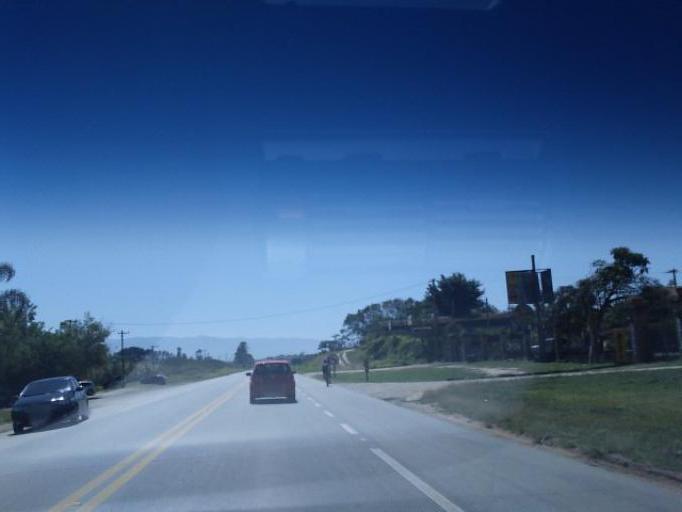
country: BR
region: Sao Paulo
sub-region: Tremembe
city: Tremembe
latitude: -22.9762
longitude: -45.6460
